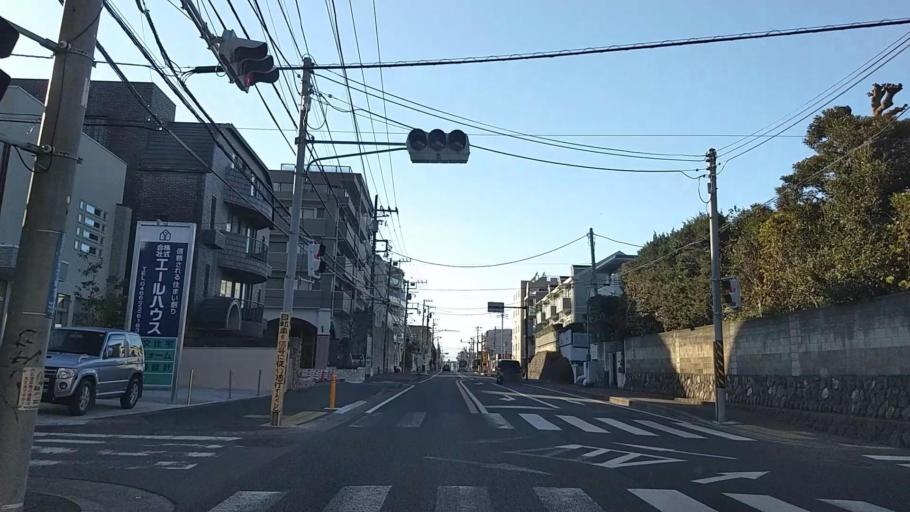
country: JP
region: Kanagawa
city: Fujisawa
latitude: 35.3276
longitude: 139.4873
